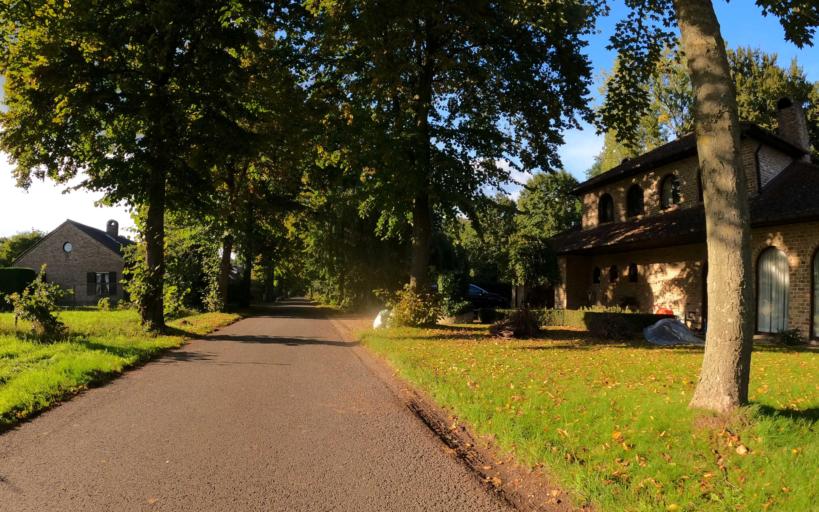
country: BE
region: Flanders
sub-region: Provincie Antwerpen
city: Zandhoven
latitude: 51.2711
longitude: 4.6499
